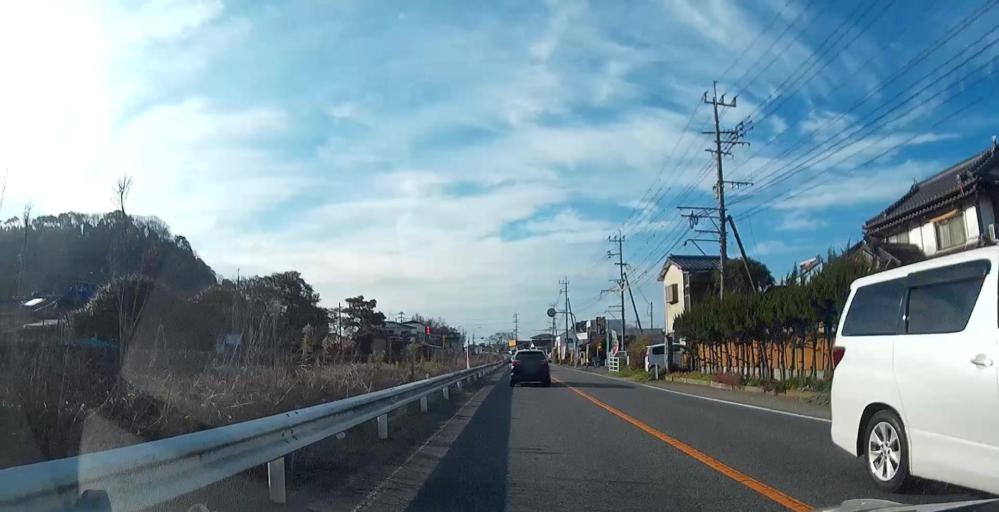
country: JP
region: Kumamoto
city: Uto
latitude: 32.7039
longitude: 130.5921
